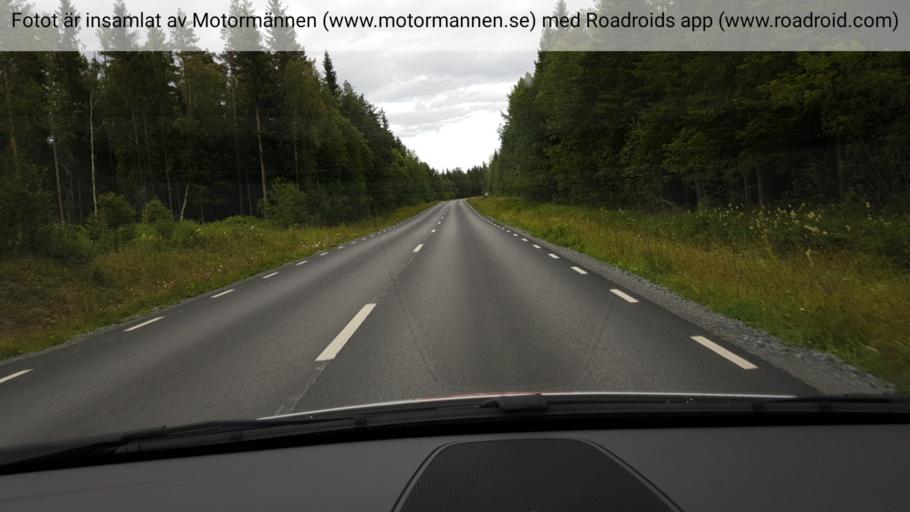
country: SE
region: Jaemtland
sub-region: Bergs Kommun
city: Hoverberg
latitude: 62.9647
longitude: 14.5064
